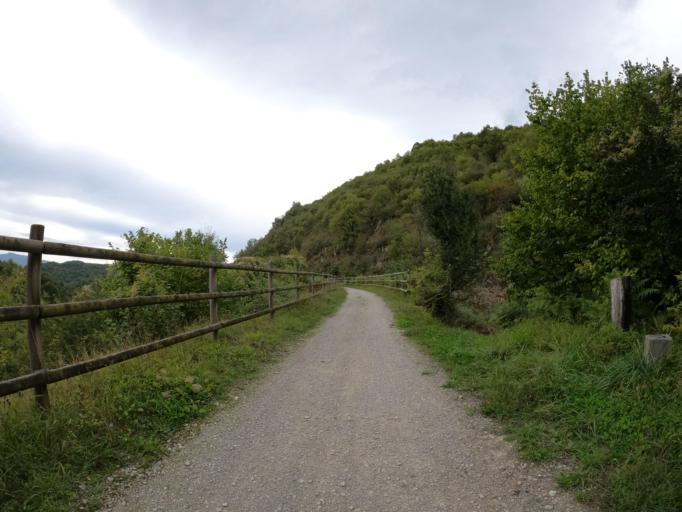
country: ES
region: Navarre
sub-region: Provincia de Navarra
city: Lekunberri
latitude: 43.0193
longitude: -1.8998
